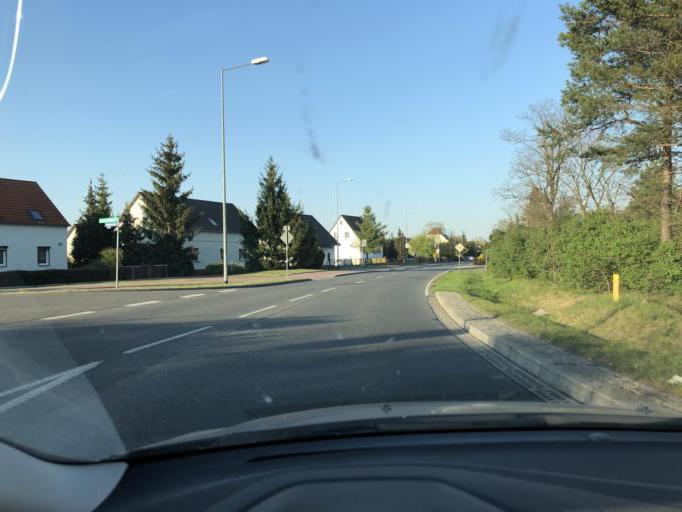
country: DE
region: Brandenburg
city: Ruhland
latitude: 51.4684
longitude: 13.8856
